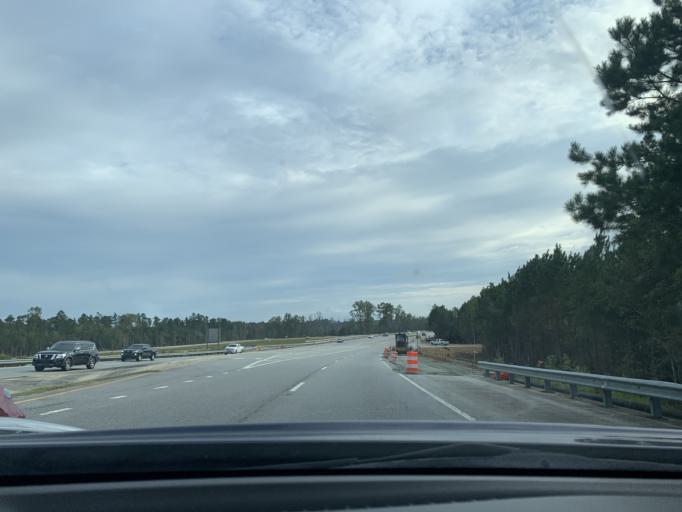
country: US
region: Georgia
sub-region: Chatham County
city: Pooler
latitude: 32.1085
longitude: -81.2664
